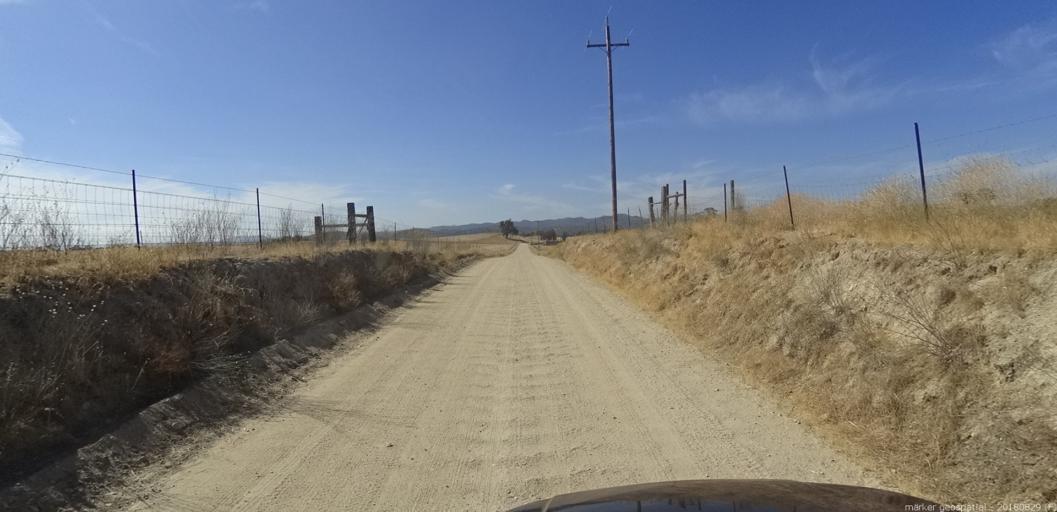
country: US
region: California
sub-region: Monterey County
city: King City
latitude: 35.9553
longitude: -121.0999
